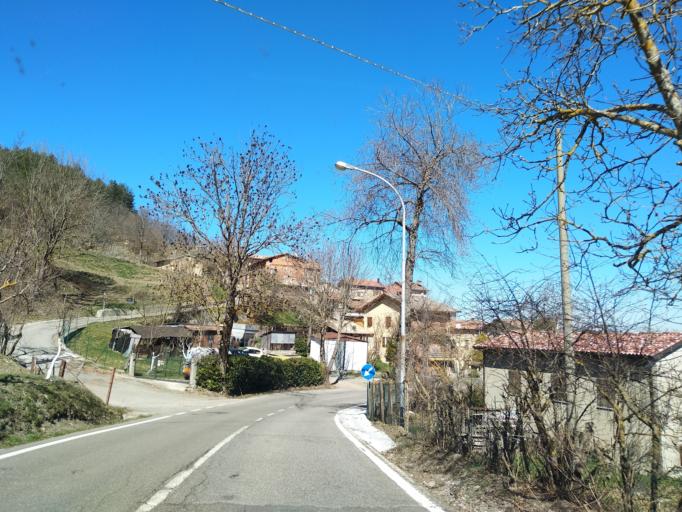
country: IT
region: Emilia-Romagna
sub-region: Provincia di Reggio Emilia
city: Ramiseto
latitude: 44.4126
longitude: 10.3013
